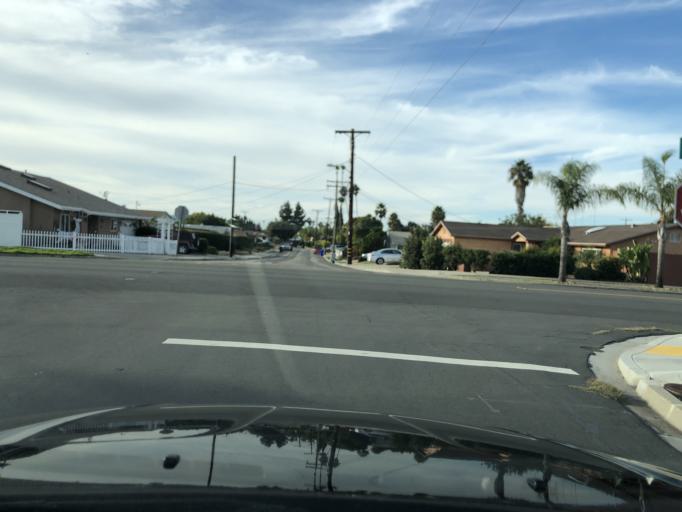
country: US
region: California
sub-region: San Diego County
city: La Jolla
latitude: 32.8247
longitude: -117.1736
